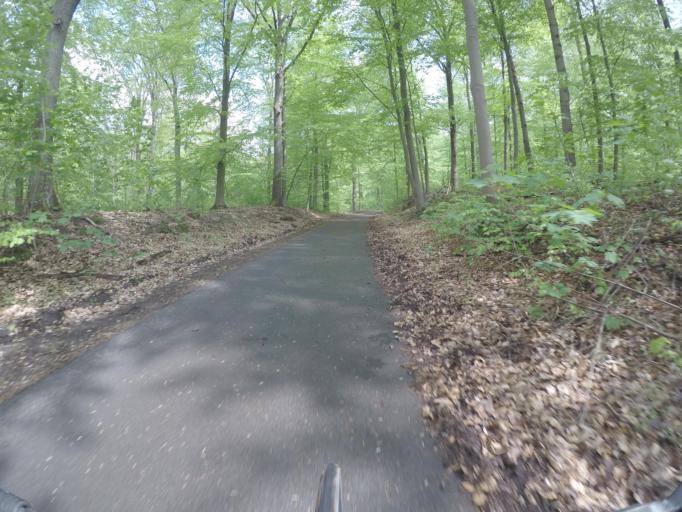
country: DE
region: Brandenburg
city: Joachimsthal
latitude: 52.9601
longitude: 13.7270
